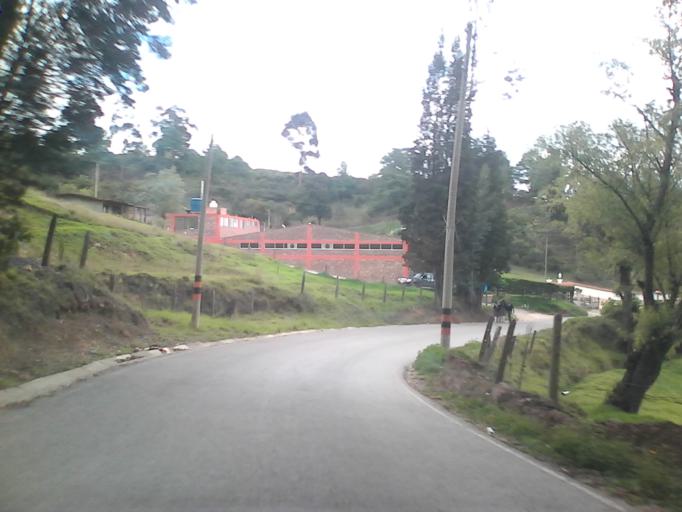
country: CO
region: Boyaca
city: Duitama
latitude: 5.7930
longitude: -73.0601
